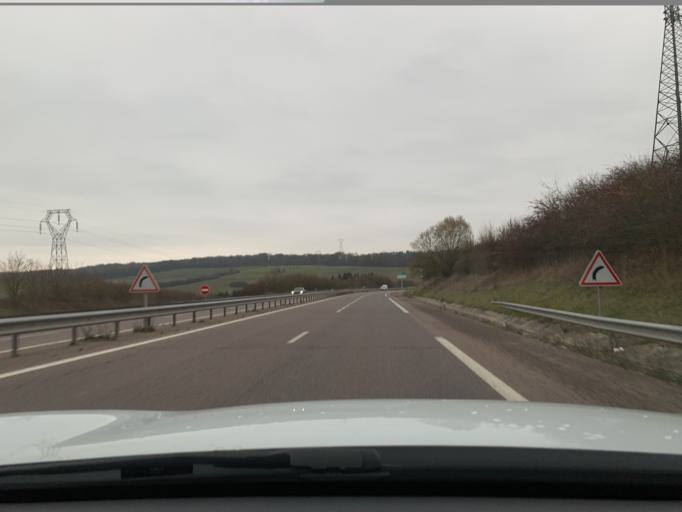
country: FR
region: Lorraine
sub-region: Departement de la Moselle
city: Sarreguemines
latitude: 49.1064
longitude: 7.0291
